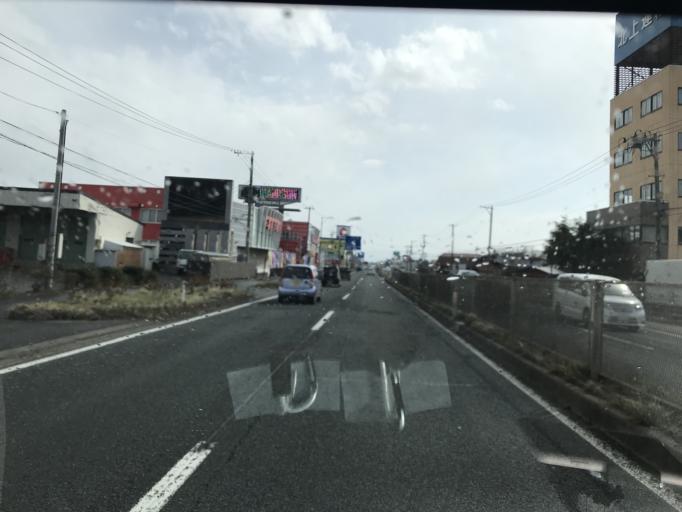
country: JP
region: Iwate
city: Kitakami
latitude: 39.3030
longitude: 141.1083
